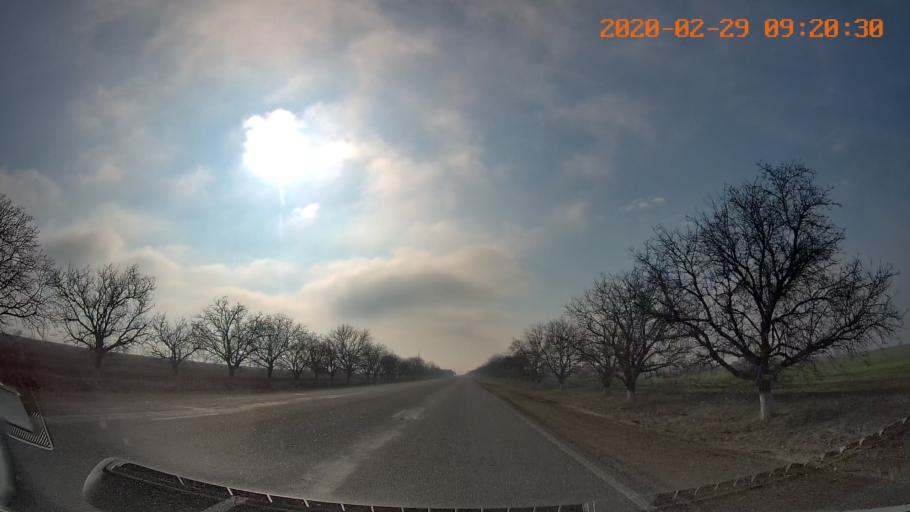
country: MD
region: Telenesti
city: Pervomaisc
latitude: 46.7481
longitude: 29.9495
